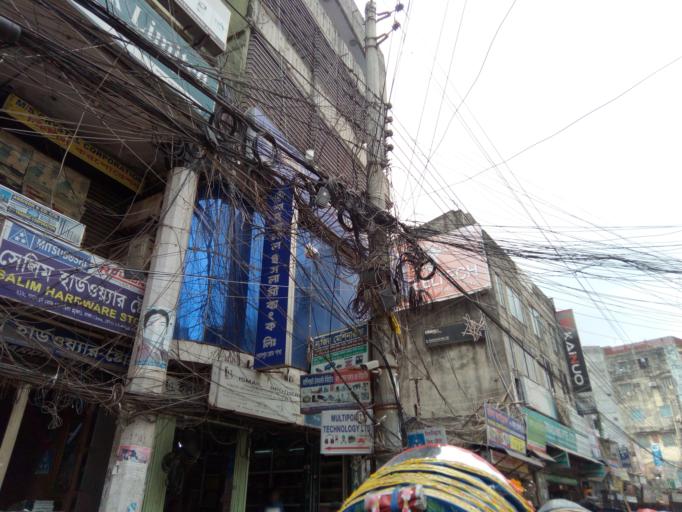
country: BD
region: Dhaka
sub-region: Dhaka
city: Dhaka
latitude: 23.7178
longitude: 90.4113
